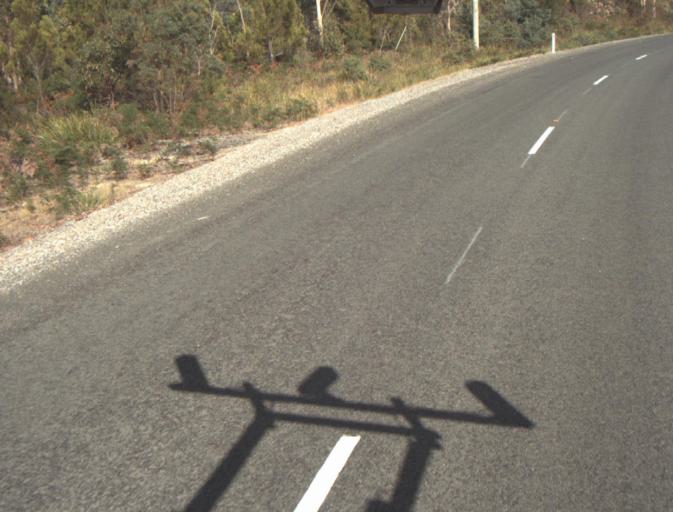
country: AU
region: Tasmania
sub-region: Dorset
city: Bridport
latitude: -41.1366
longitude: 147.2246
